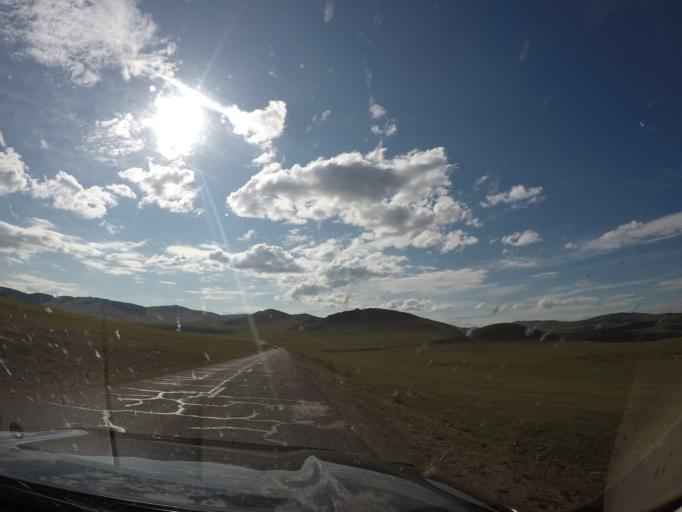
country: MN
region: Hentiy
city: Modot
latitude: 47.7523
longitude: 108.9508
